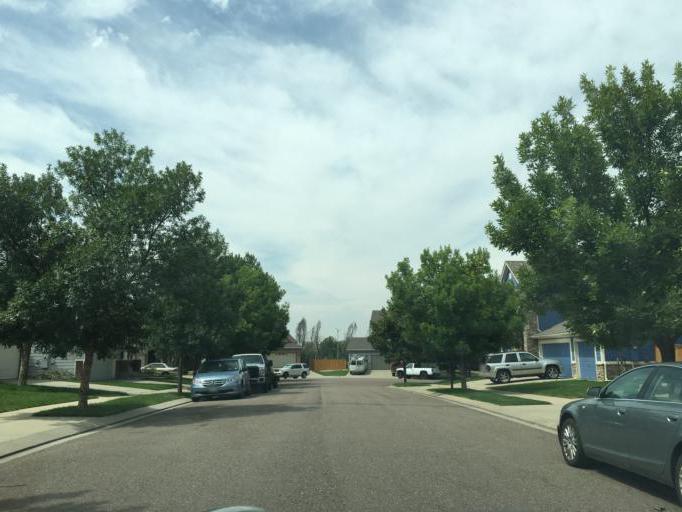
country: US
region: Colorado
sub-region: Adams County
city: Aurora
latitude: 39.7268
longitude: -104.8084
